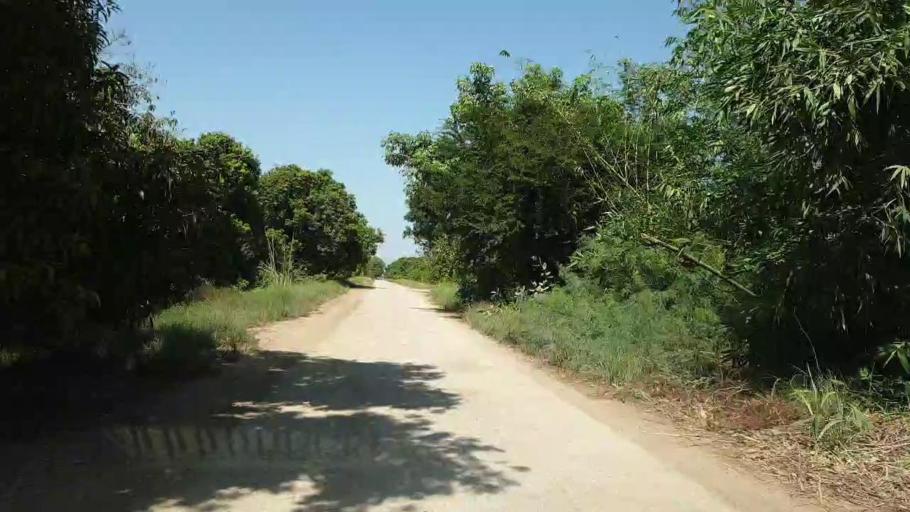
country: PK
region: Sindh
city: Tando Jam
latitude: 25.4331
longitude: 68.4599
